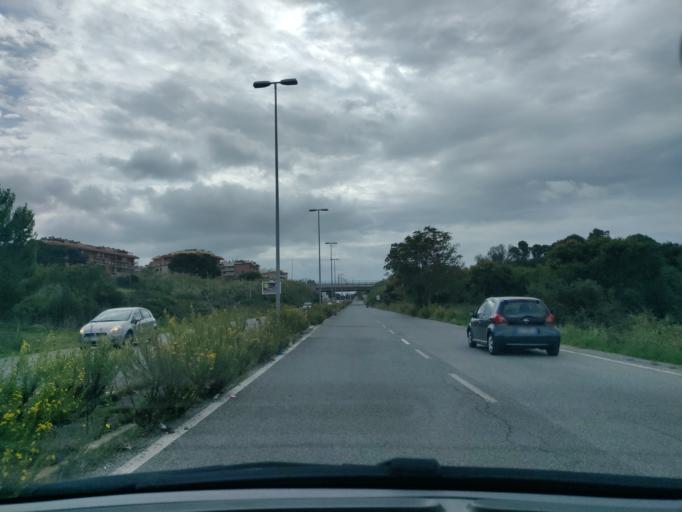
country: IT
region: Latium
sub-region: Citta metropolitana di Roma Capitale
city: Civitavecchia
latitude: 42.1047
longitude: 11.7911
